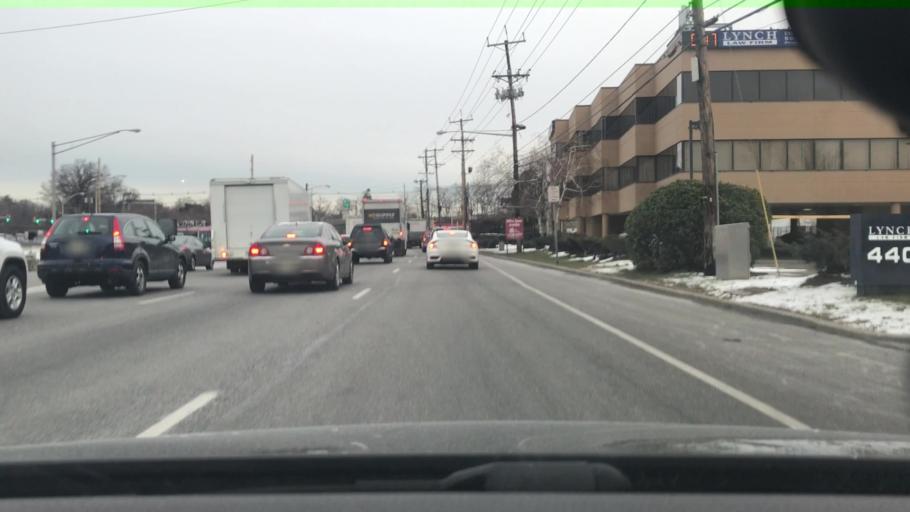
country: US
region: New Jersey
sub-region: Bergen County
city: Hasbrouck Heights
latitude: 40.8635
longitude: -74.0644
